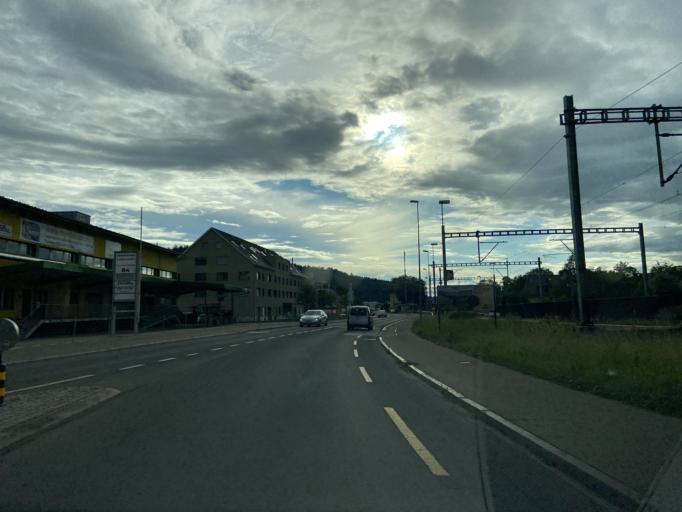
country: CH
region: Zurich
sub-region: Bezirk Winterthur
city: Elsau-Raeterschen / Raeterschen
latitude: 47.4981
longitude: 8.7978
